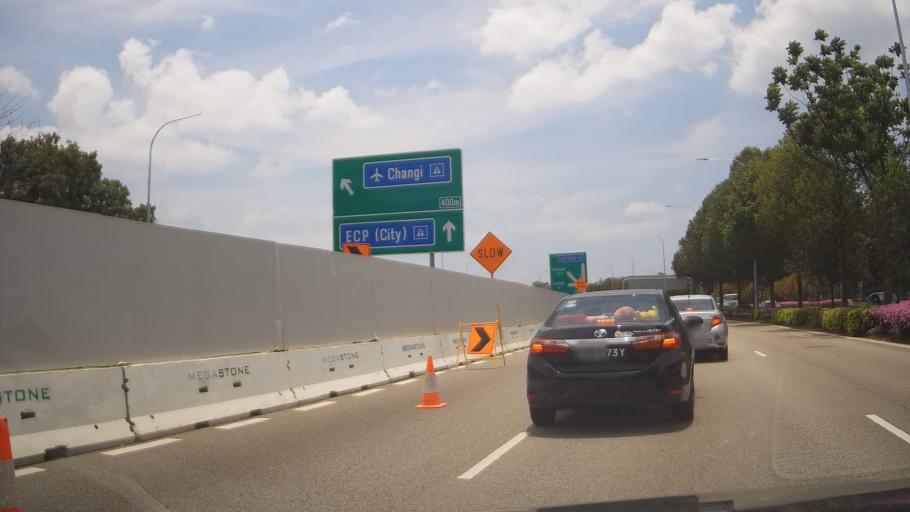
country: SG
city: Singapore
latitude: 1.3410
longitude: 103.9712
